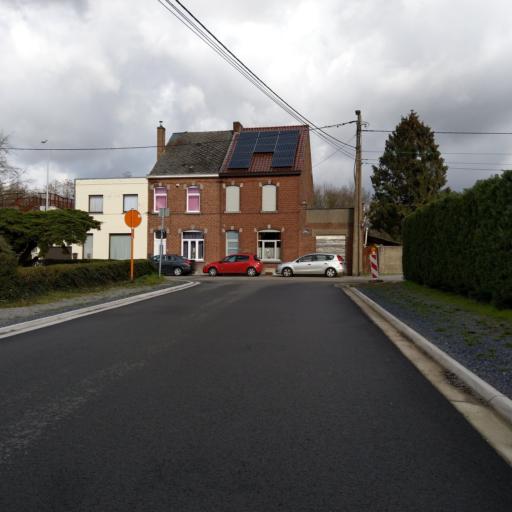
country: BE
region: Wallonia
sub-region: Province du Hainaut
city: Mons
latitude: 50.4801
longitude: 3.9437
